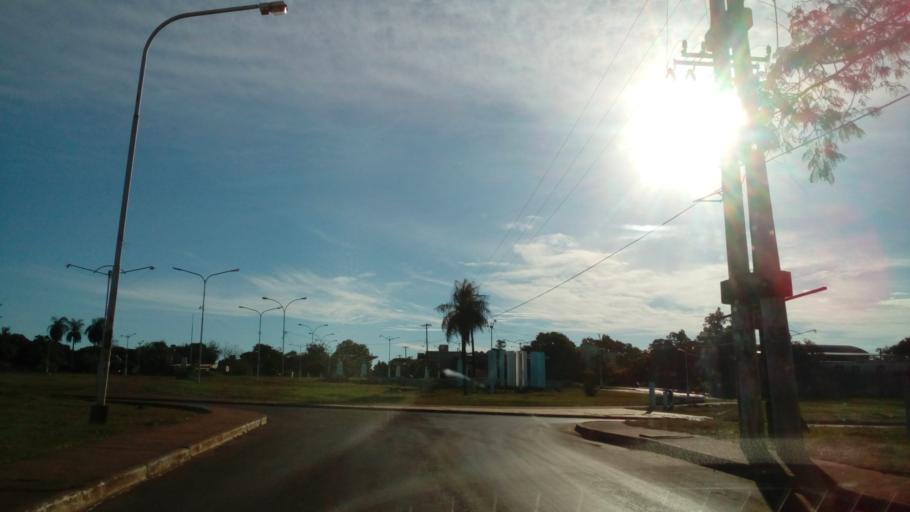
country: AR
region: Misiones
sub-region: Departamento de Capital
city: Posadas
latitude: -27.4272
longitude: -55.8786
